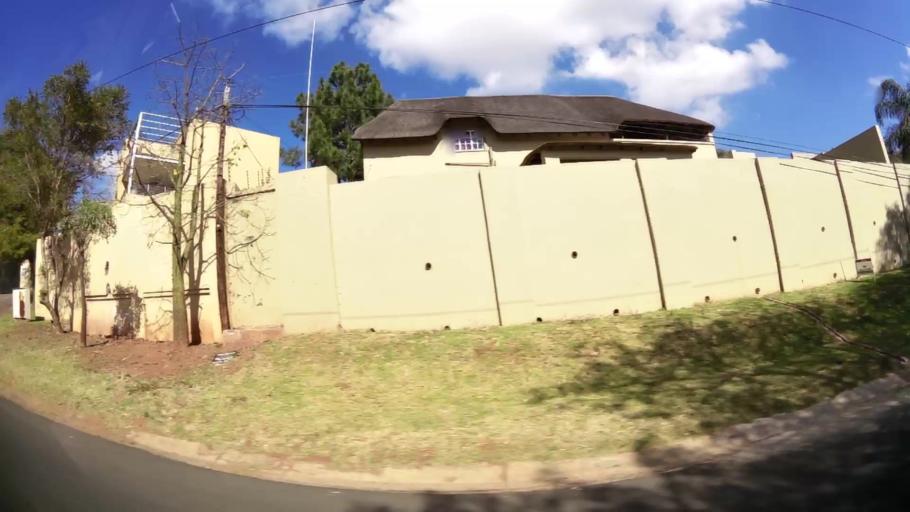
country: ZA
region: Gauteng
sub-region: City of Johannesburg Metropolitan Municipality
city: Roodepoort
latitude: -26.1125
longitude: 27.8391
